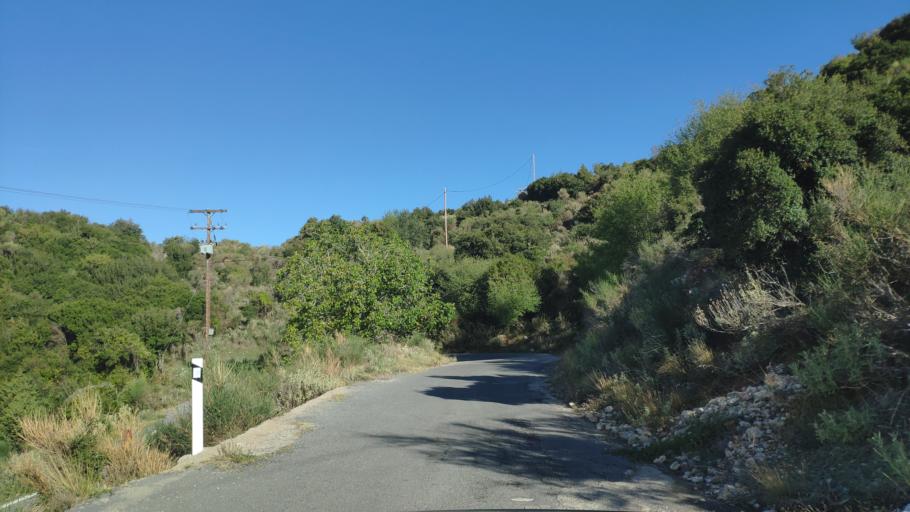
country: GR
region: Peloponnese
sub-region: Nomos Arkadias
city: Dimitsana
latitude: 37.5518
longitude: 22.0628
